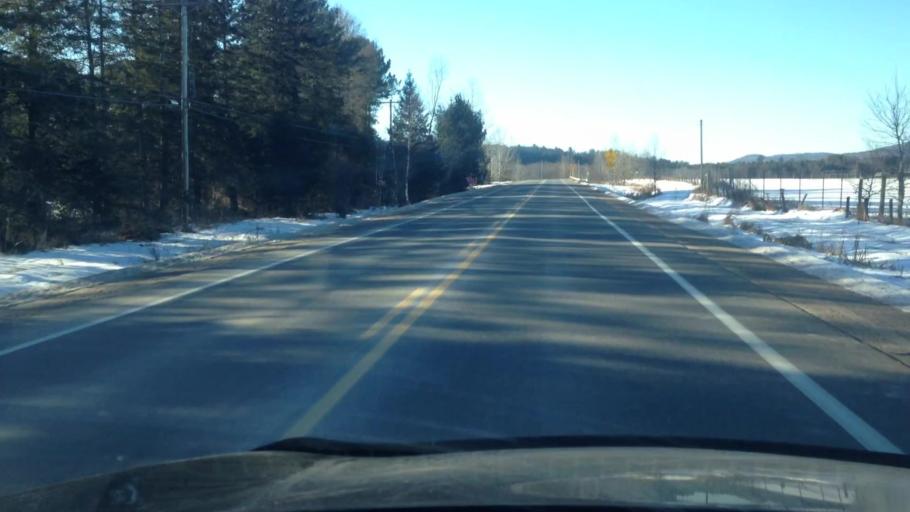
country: CA
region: Quebec
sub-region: Laurentides
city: Mont-Tremblant
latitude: 45.9628
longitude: -74.5911
